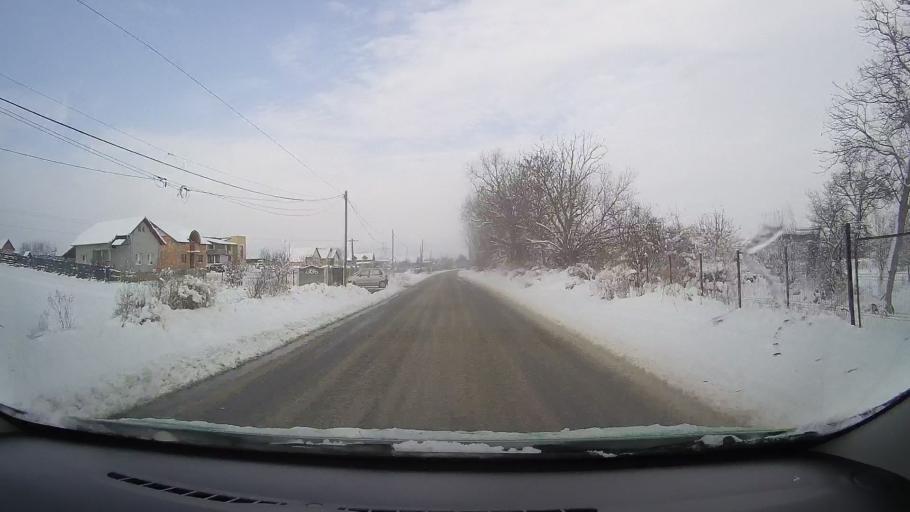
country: RO
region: Alba
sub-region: Comuna Pianu
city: Pianu de Jos
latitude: 45.9433
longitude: 23.4819
